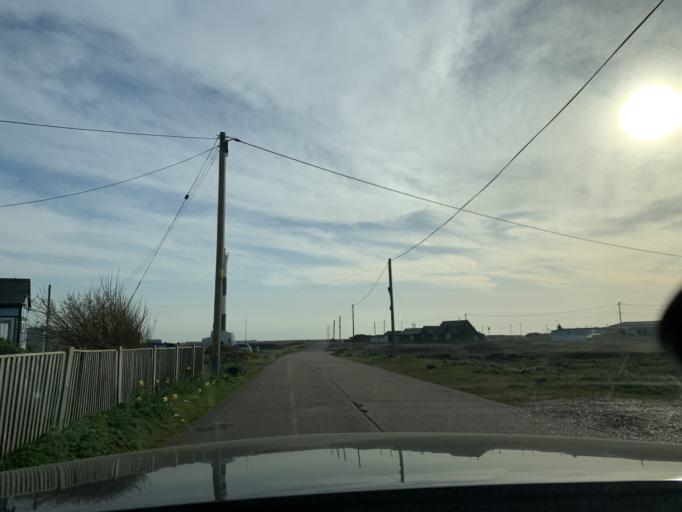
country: GB
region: England
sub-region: Kent
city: Lydd
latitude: 50.9154
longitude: 0.9770
